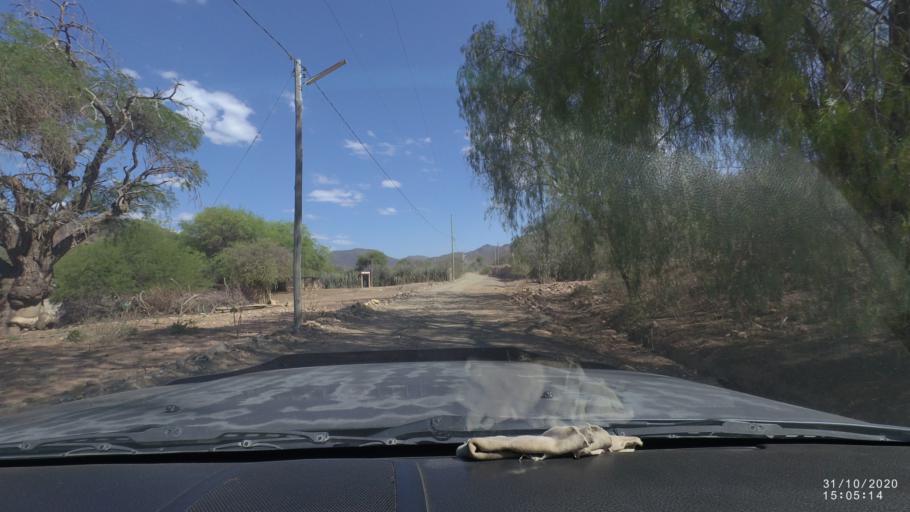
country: BO
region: Cochabamba
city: Aiquile
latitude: -18.2886
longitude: -64.7997
